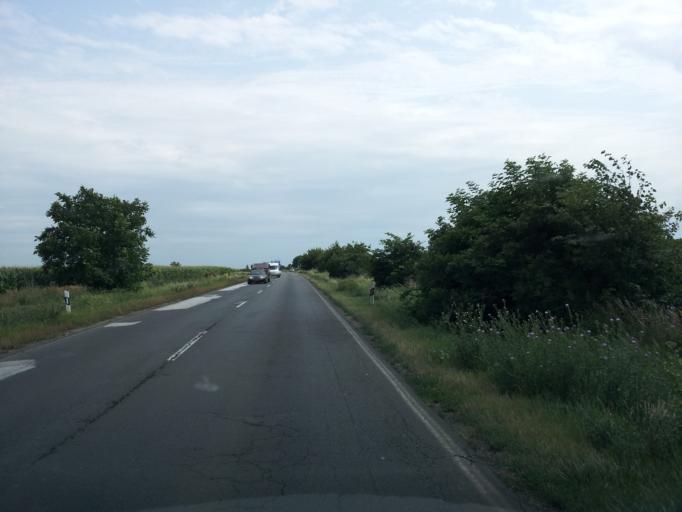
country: HU
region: Fejer
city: Lepseny
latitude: 46.9684
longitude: 18.2077
